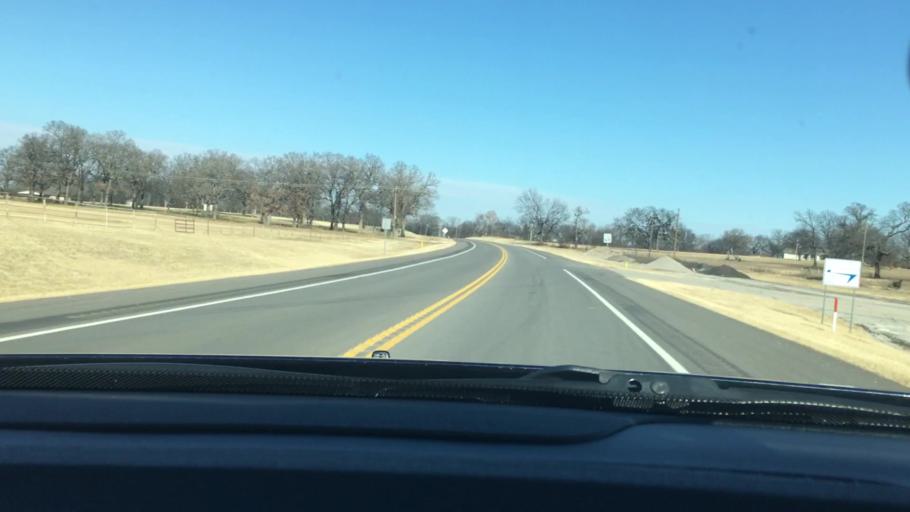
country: US
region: Oklahoma
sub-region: Murray County
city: Davis
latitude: 34.5157
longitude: -97.1213
